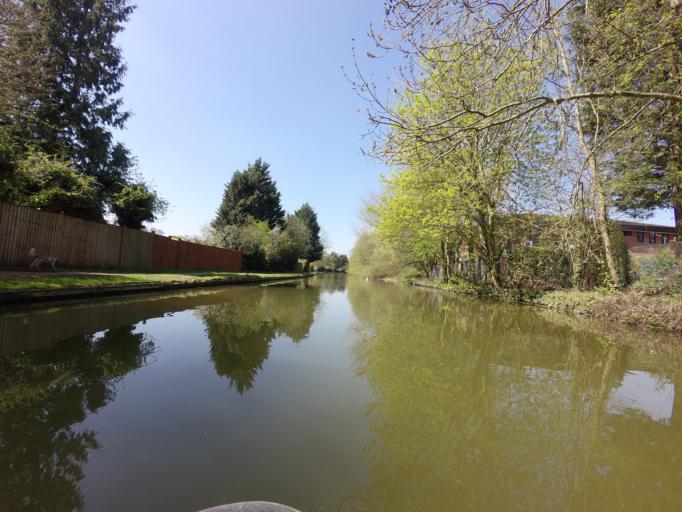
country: GB
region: England
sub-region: Hertfordshire
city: Berkhamsted
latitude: 51.7680
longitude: -0.5832
